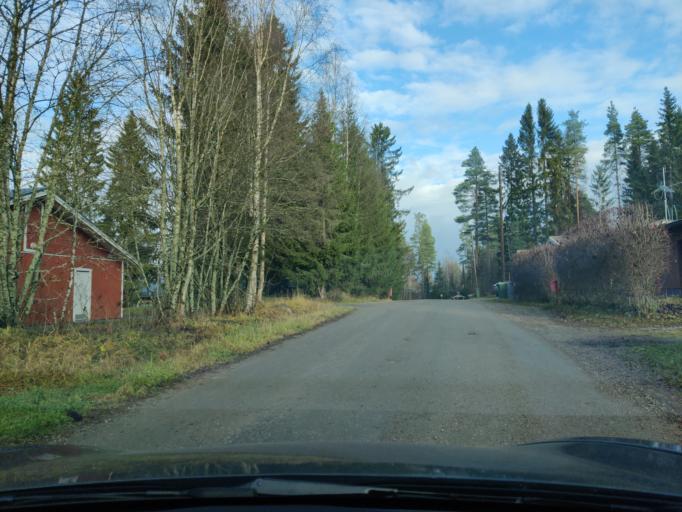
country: FI
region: Northern Savo
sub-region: Ylae-Savo
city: Kiuruvesi
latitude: 63.6441
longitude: 26.6353
